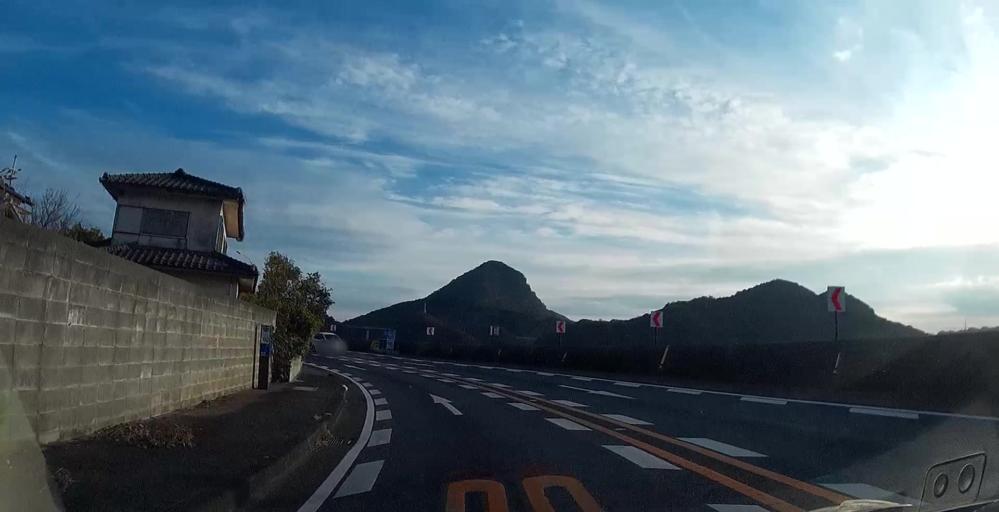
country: JP
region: Nagasaki
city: Shimabara
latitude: 32.6239
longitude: 130.4510
